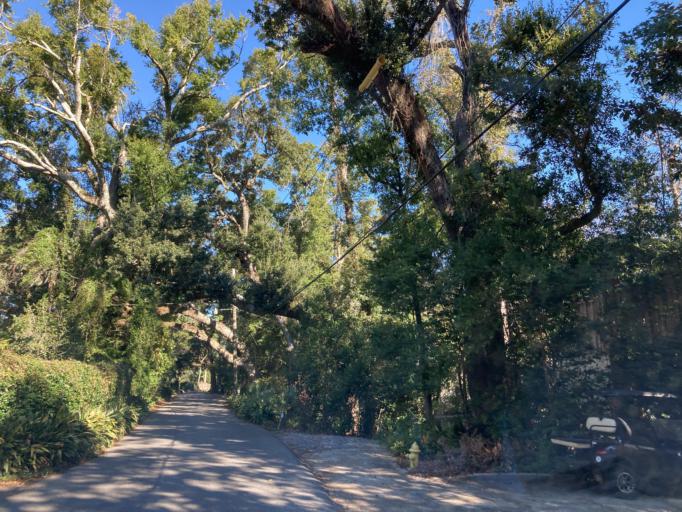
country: US
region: Mississippi
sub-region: Jackson County
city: Gulf Hills
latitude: 30.4163
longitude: -88.8420
